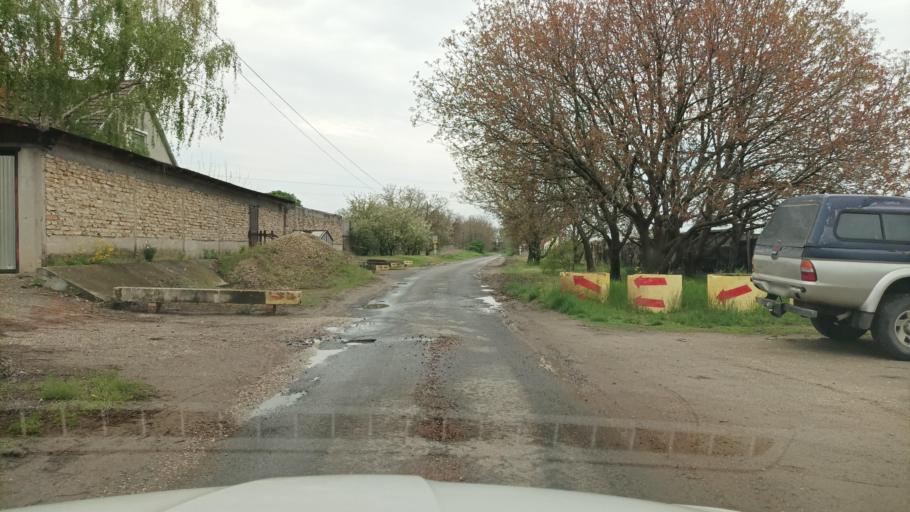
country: HU
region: Pest
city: Nagykoros
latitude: 47.0071
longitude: 19.7967
